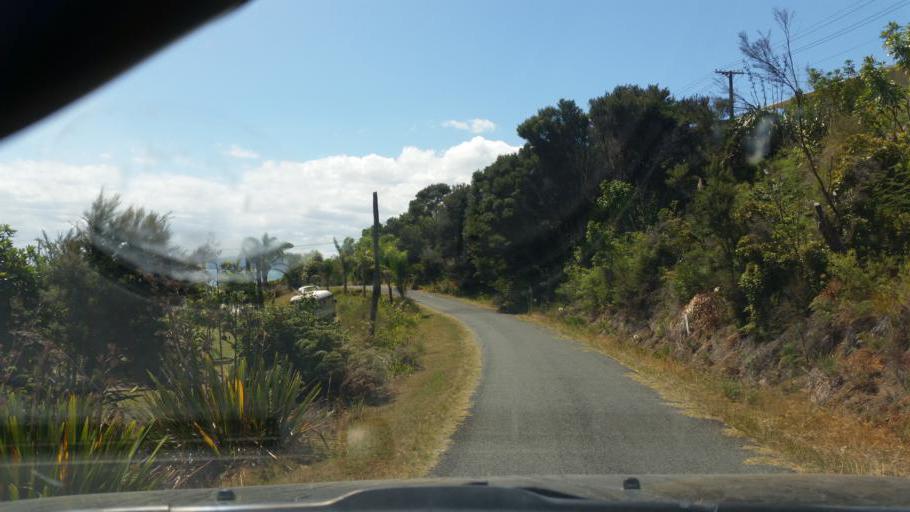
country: NZ
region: Northland
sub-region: Kaipara District
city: Dargaville
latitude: -36.2493
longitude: 174.1004
